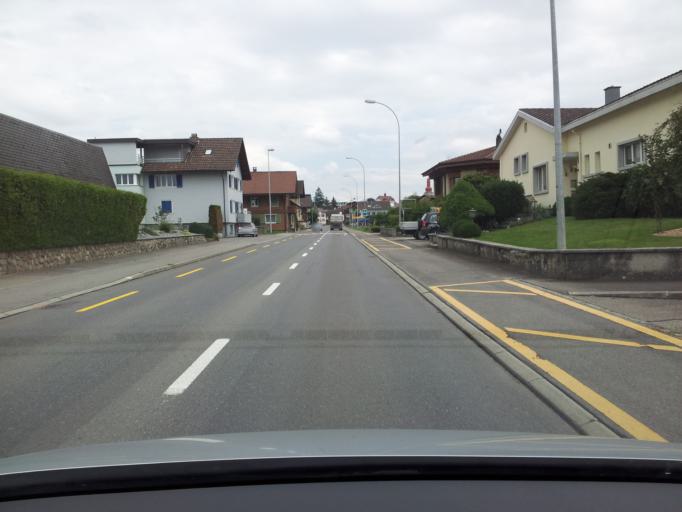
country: CH
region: Lucerne
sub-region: Sursee District
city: Buttisholz
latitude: 47.1117
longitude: 8.0887
